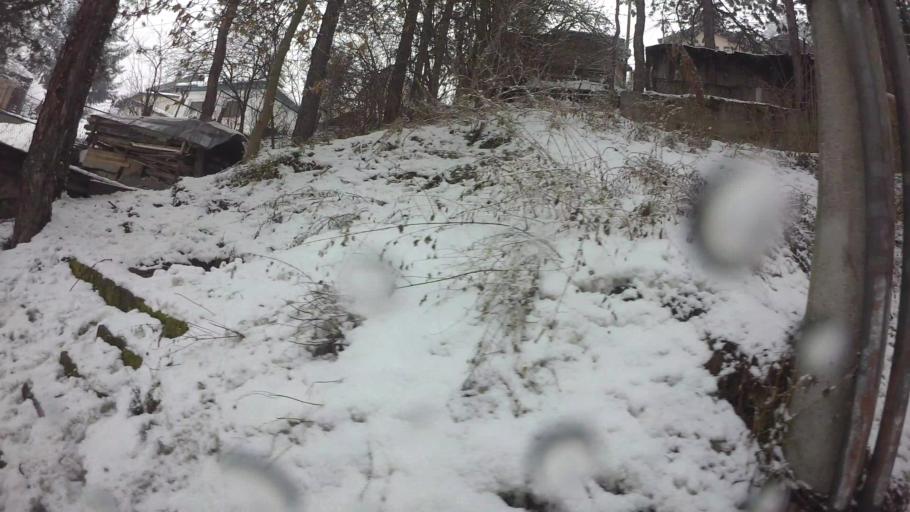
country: BA
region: Federation of Bosnia and Herzegovina
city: Kobilja Glava
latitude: 43.8502
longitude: 18.4283
